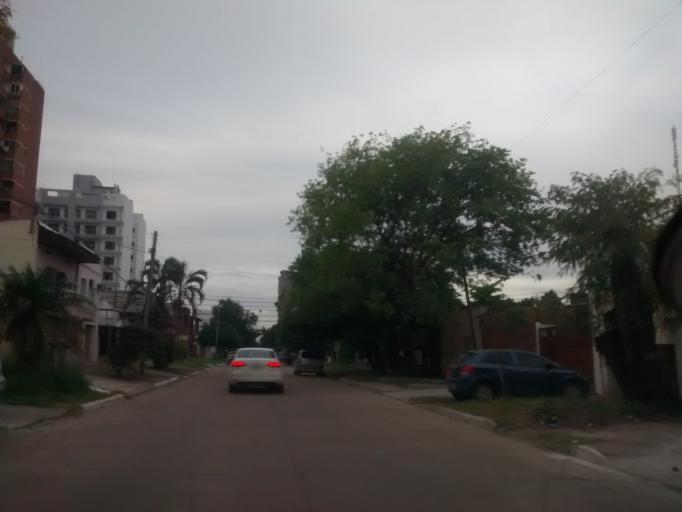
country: AR
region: Chaco
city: Resistencia
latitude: -27.4571
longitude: -58.9966
